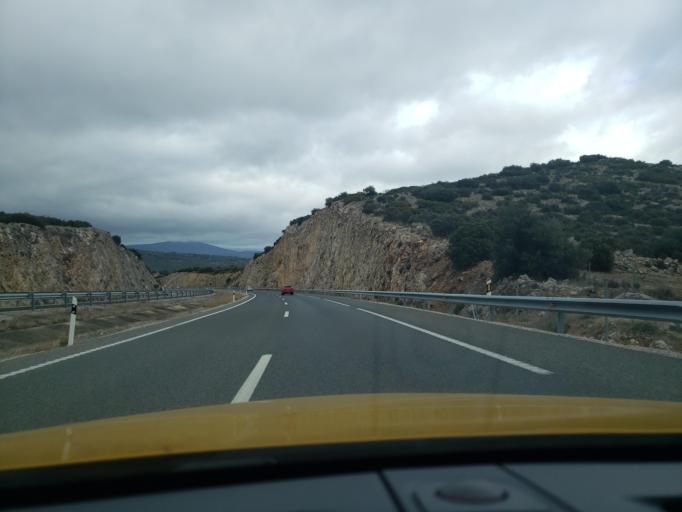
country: ES
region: Andalusia
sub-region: Provincia de Granada
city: Iznalloz
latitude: 37.4417
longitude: -3.5589
